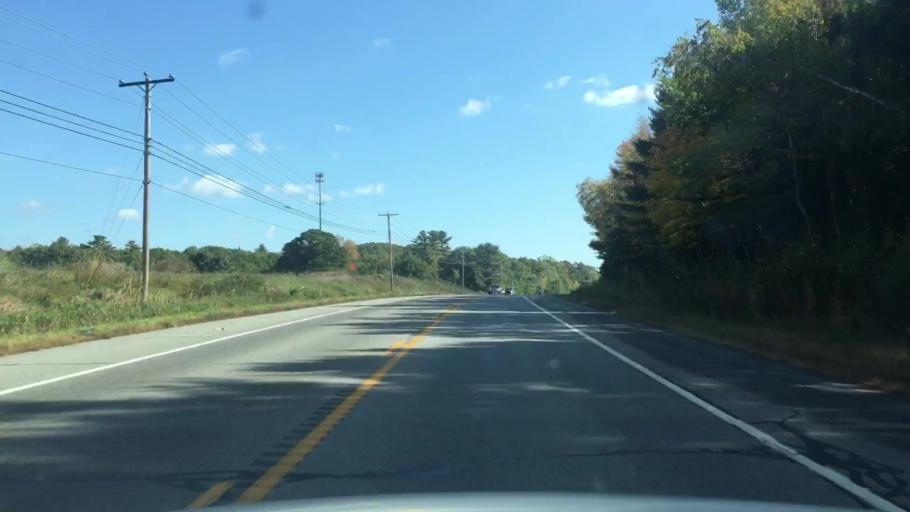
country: US
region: Maine
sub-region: Knox County
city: Warren
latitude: 44.1203
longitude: -69.2772
